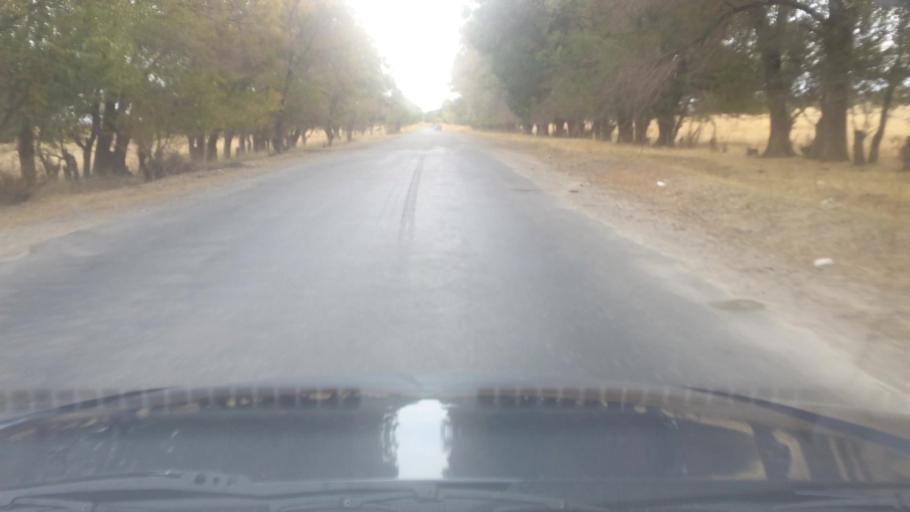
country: KG
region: Ysyk-Koel
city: Balykchy
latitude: 42.3086
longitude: 76.4637
